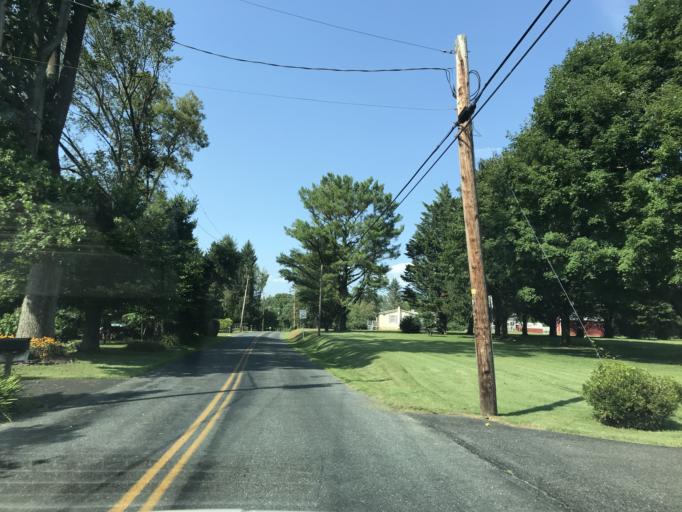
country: US
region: Maryland
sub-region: Harford County
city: South Bel Air
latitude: 39.6264
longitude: -76.2758
